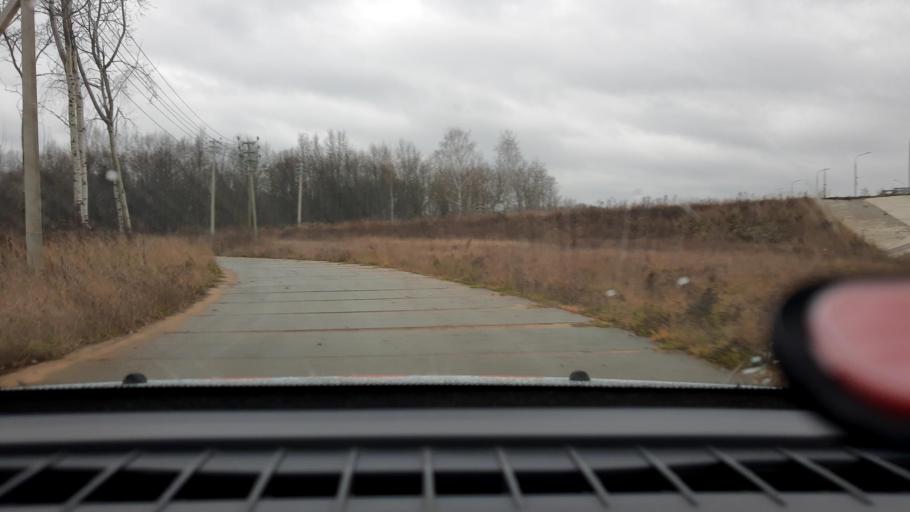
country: RU
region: Nizjnij Novgorod
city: Neklyudovo
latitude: 56.3796
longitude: 43.9588
